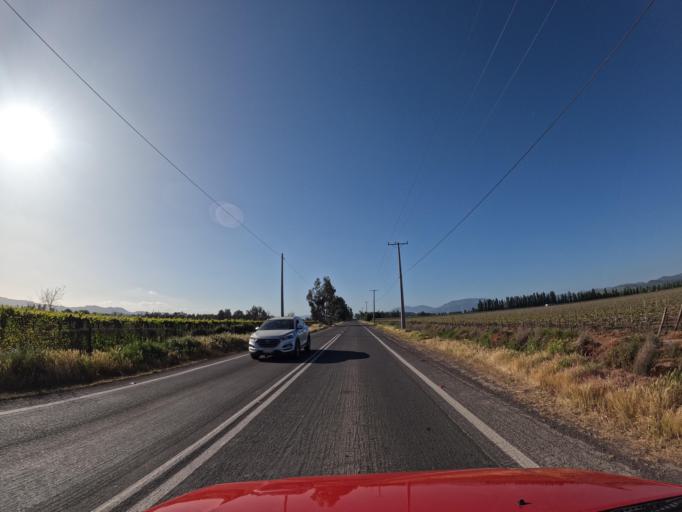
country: CL
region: Maule
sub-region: Provincia de Curico
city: Teno
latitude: -34.7648
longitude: -71.2373
